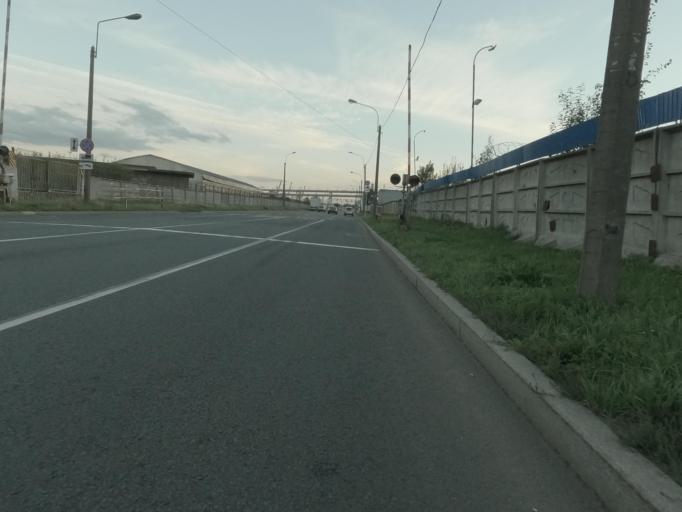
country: RU
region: St.-Petersburg
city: Vasyl'evsky Ostrov
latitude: 59.9074
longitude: 30.2374
